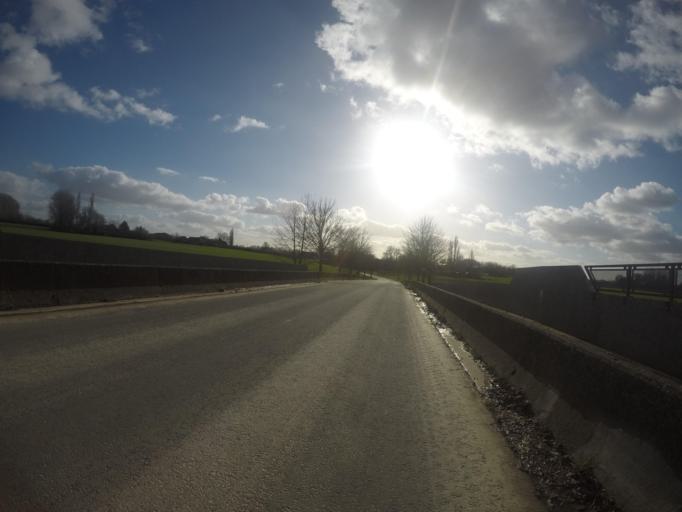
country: BE
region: Wallonia
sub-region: Province du Brabant Wallon
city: Rebecq-Rognon
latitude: 50.6743
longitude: 4.0849
